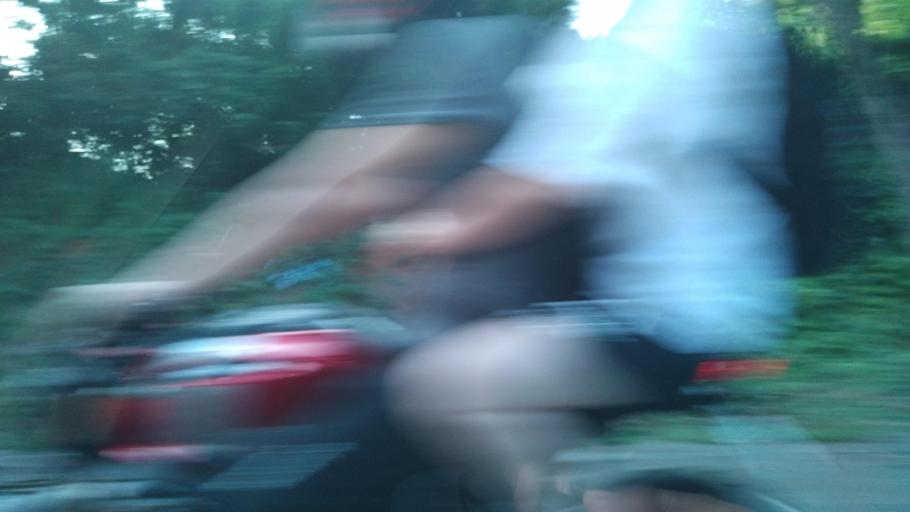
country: TW
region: Taipei
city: Taipei
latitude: 25.2746
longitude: 121.5137
